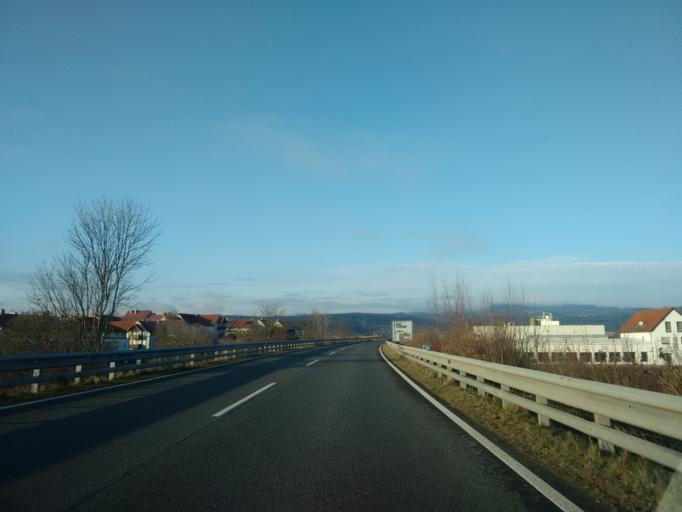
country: AT
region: Lower Austria
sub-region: Politischer Bezirk Melk
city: Melk
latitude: 48.2285
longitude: 15.3490
